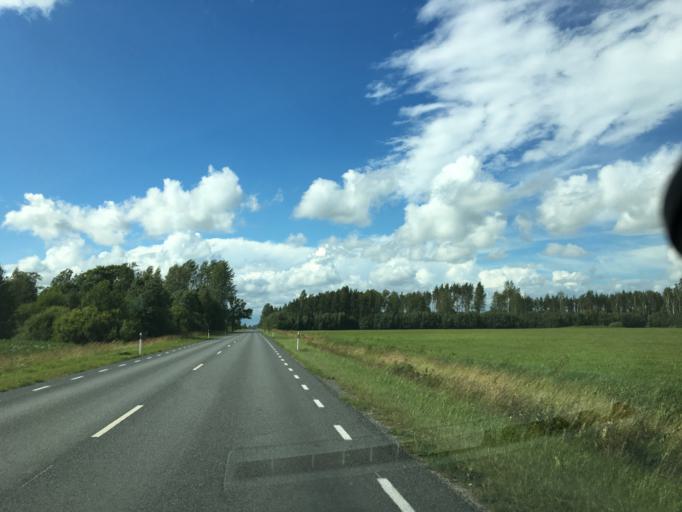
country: EE
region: Paernumaa
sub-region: Vaendra vald (alev)
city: Vandra
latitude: 58.5834
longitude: 25.1776
